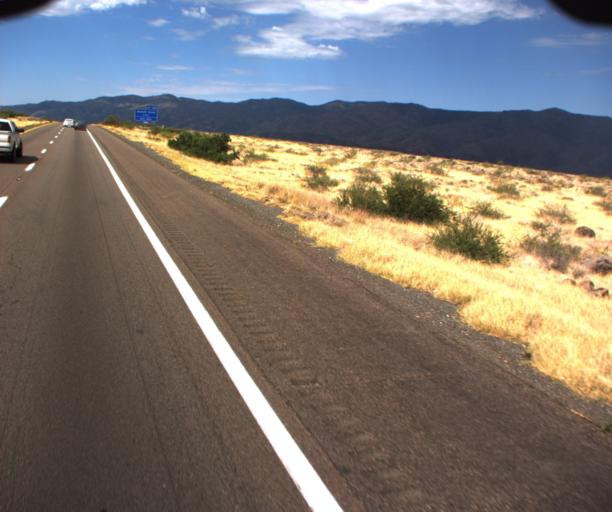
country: US
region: Arizona
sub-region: Yavapai County
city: Cordes Lakes
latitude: 34.2092
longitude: -112.1183
